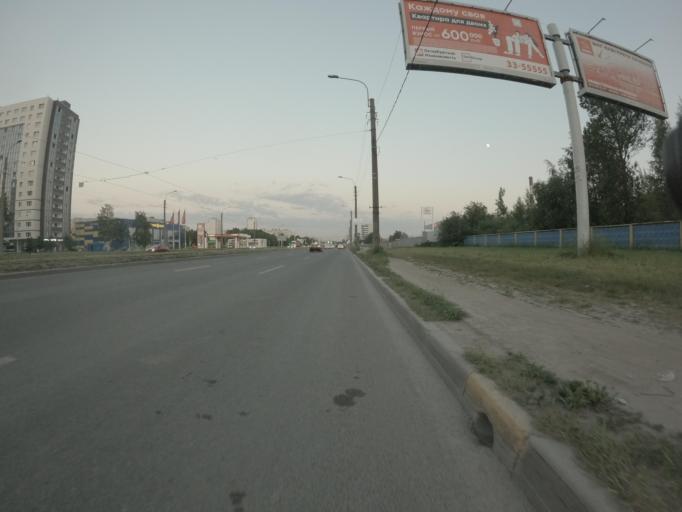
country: RU
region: St.-Petersburg
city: Obukhovo
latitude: 59.8959
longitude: 30.4612
